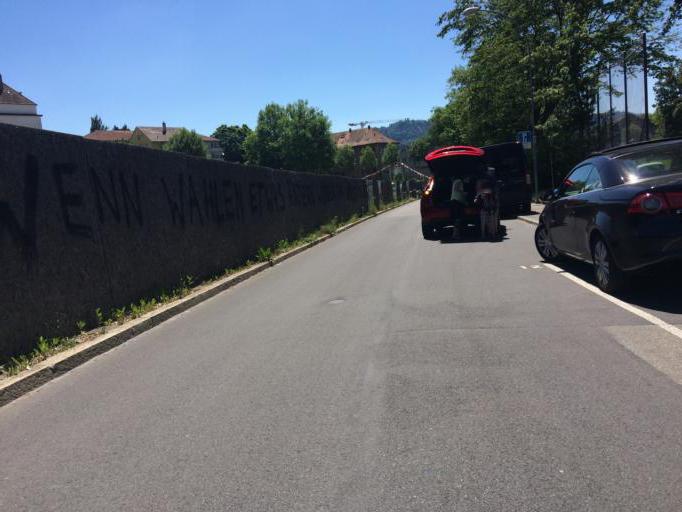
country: CH
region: Bern
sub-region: Bern-Mittelland District
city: Koniz
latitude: 46.9474
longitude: 7.4148
